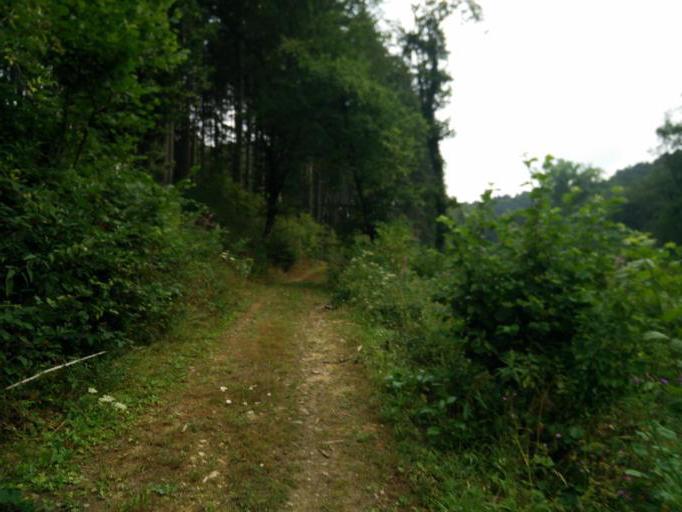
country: LU
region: Luxembourg
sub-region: Canton de Capellen
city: Mamer
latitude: 49.6352
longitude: 6.0461
